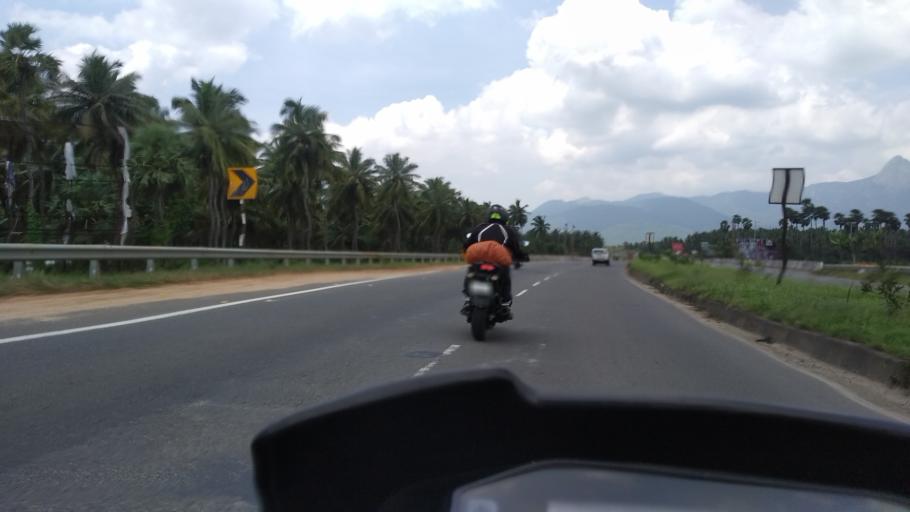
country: IN
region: Tamil Nadu
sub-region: Coimbatore
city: Madukkarai
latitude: 10.8530
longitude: 76.8551
